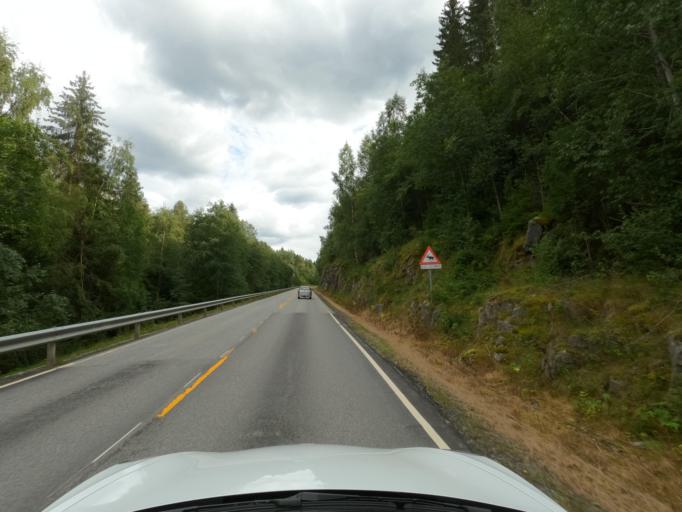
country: NO
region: Telemark
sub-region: Hjartdal
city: Sauland
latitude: 59.8285
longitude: 8.9771
